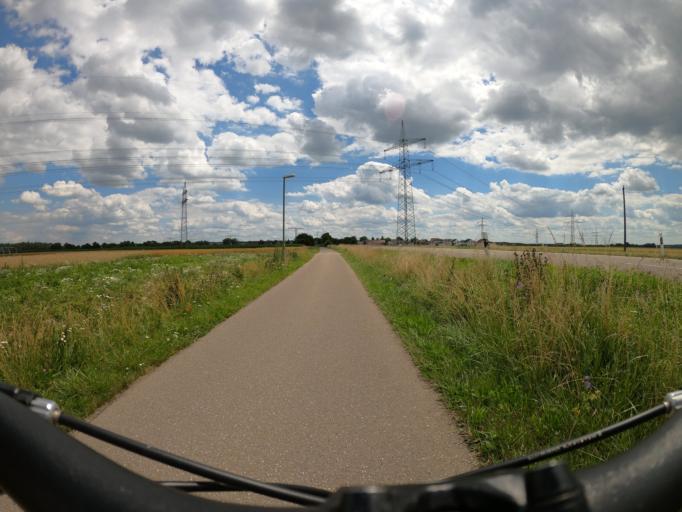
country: DE
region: Bavaria
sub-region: Swabia
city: Nersingen
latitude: 48.4221
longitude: 10.1296
